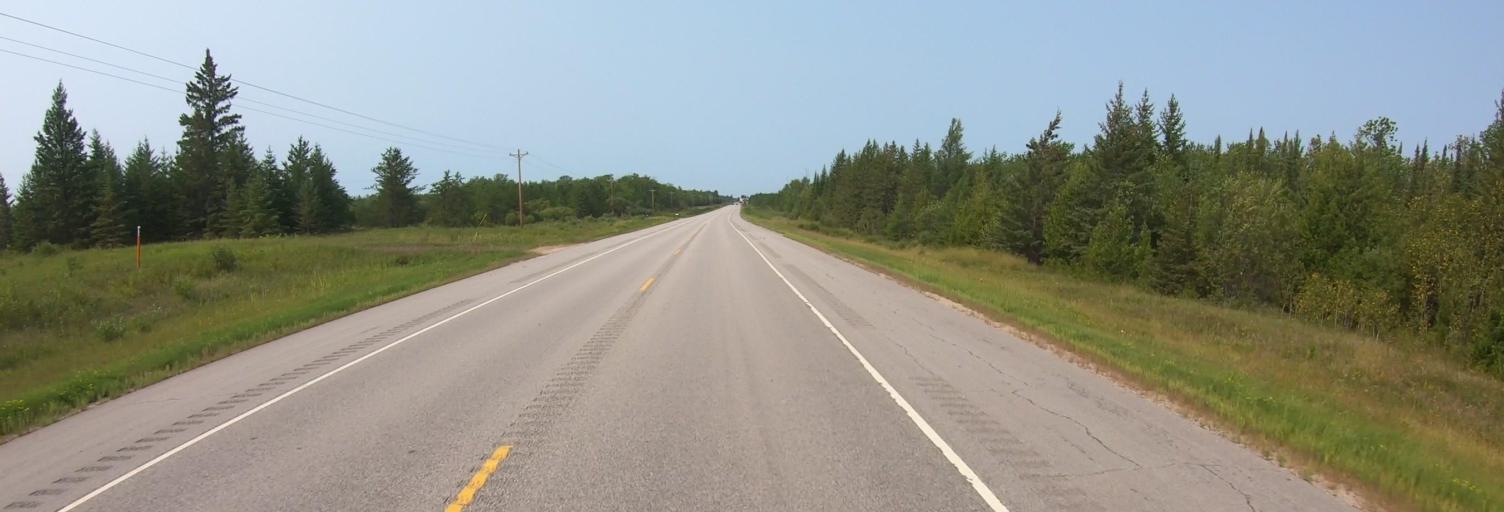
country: CA
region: Ontario
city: Fort Frances
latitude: 48.4104
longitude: -93.1781
